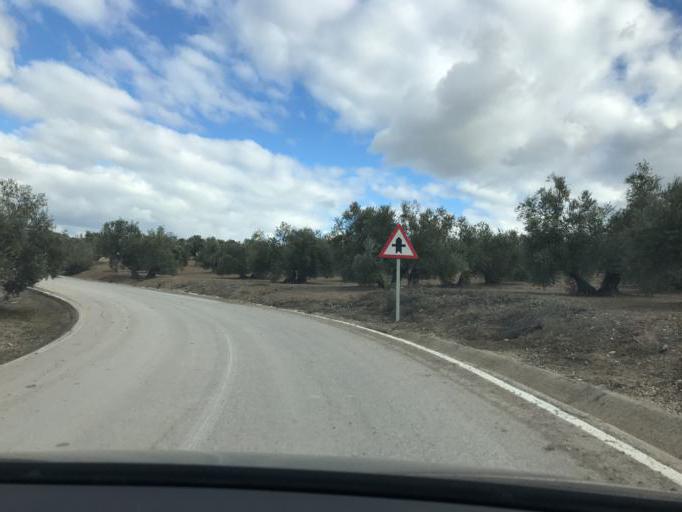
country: ES
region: Andalusia
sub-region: Provincia de Jaen
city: Baeza
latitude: 37.9665
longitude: -3.4160
